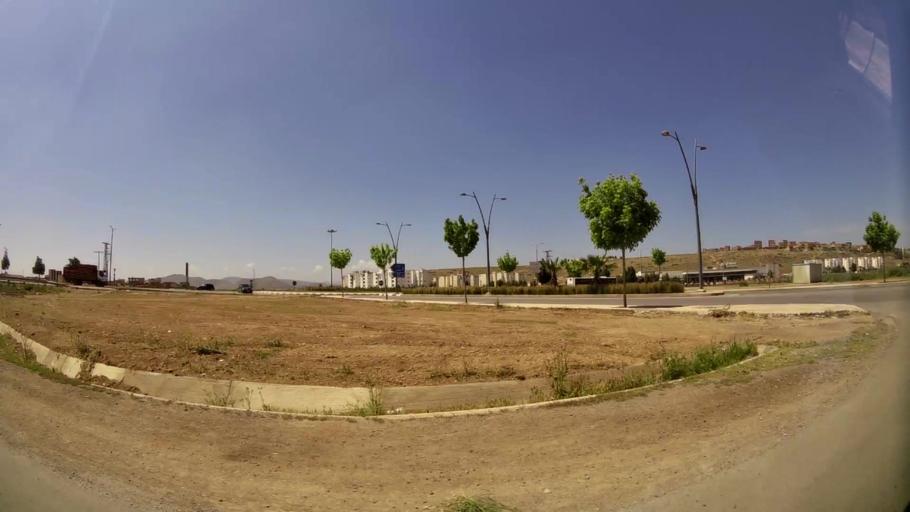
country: MA
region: Oriental
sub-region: Oujda-Angad
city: Oujda
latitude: 34.6968
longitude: -1.9406
